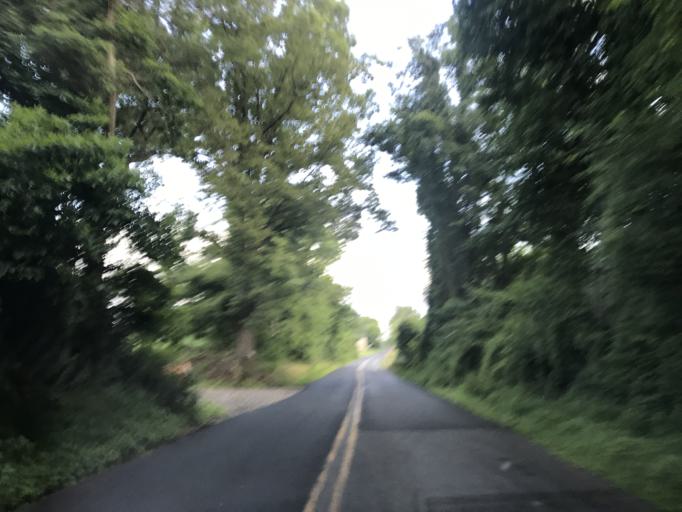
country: US
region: Maryland
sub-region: Harford County
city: Aberdeen
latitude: 39.5171
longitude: -76.2074
